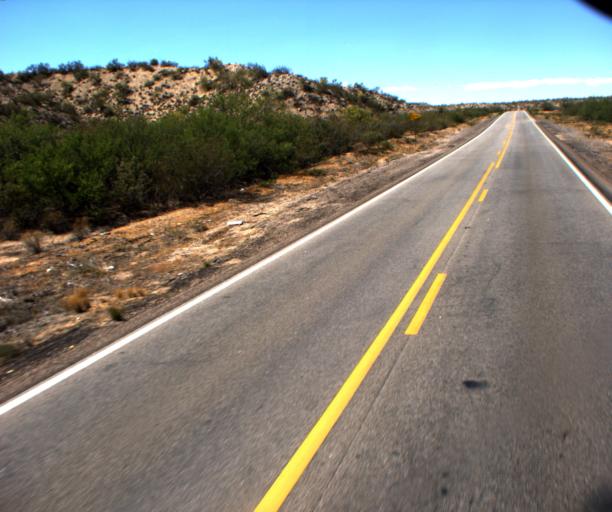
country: US
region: Arizona
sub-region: Yavapai County
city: Bagdad
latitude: 34.7833
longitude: -113.6231
